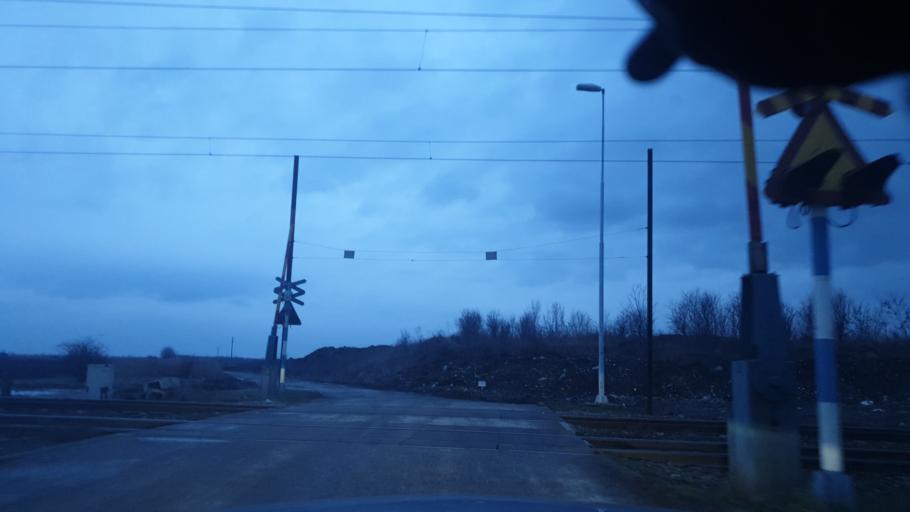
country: RS
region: Autonomna Pokrajina Vojvodina
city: Nova Pazova
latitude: 44.9350
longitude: 20.2145
